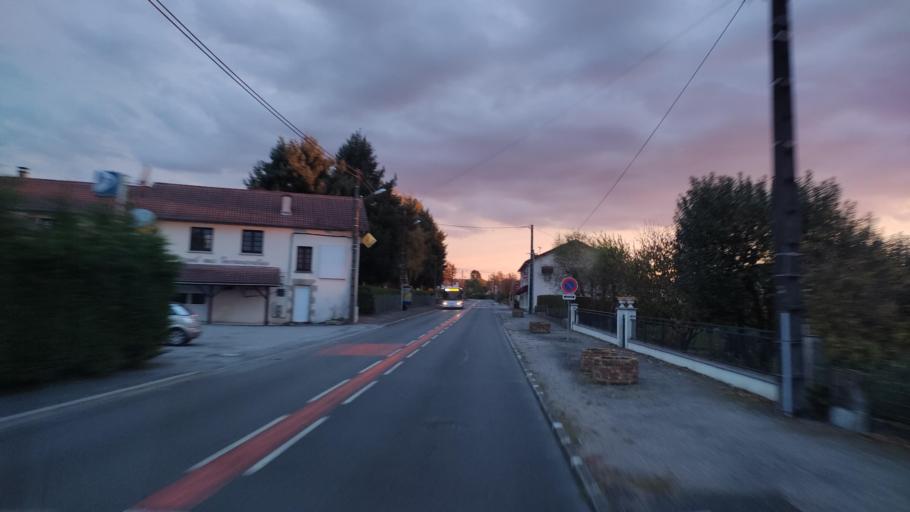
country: FR
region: Limousin
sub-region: Departement de la Haute-Vienne
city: Rilhac-Rancon
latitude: 45.9233
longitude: 1.3419
